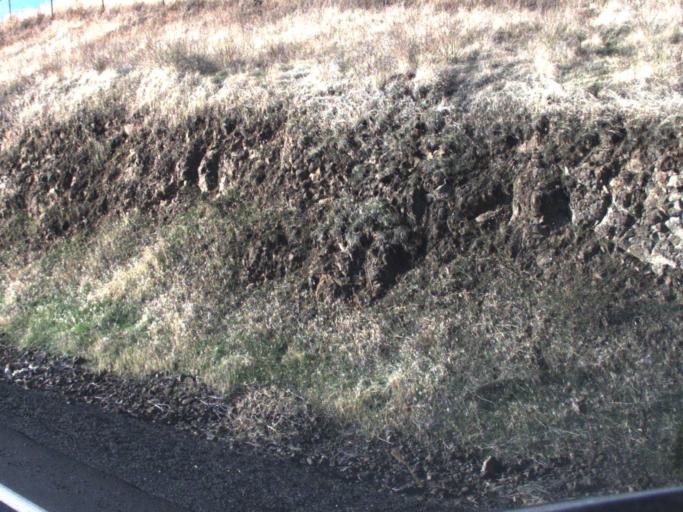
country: US
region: Washington
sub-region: Whitman County
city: Colfax
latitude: 46.7152
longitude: -117.4691
